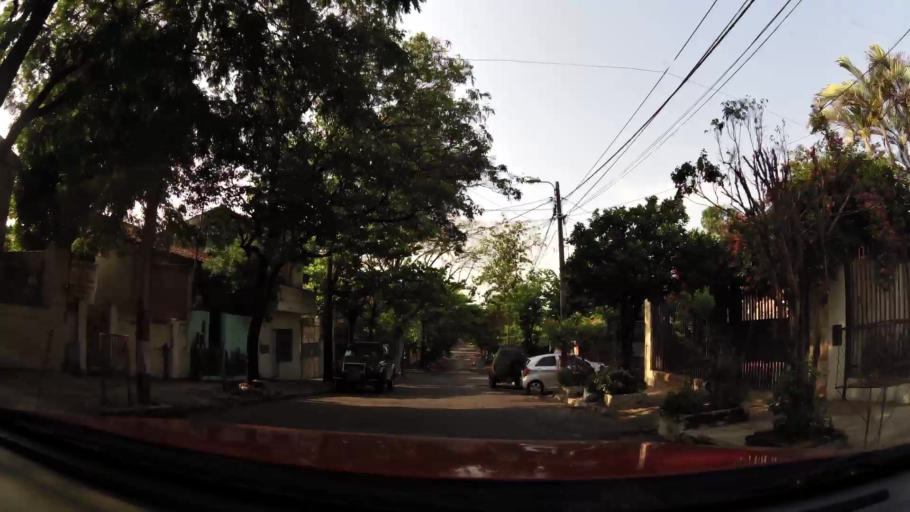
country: PY
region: Presidente Hayes
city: Nanawa
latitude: -25.2851
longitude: -57.6641
